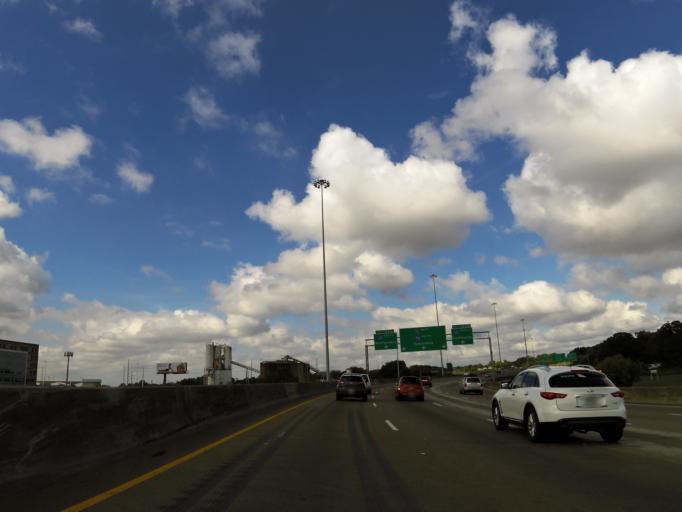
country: US
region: Alabama
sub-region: Jefferson County
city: Birmingham
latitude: 33.5201
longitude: -86.8174
